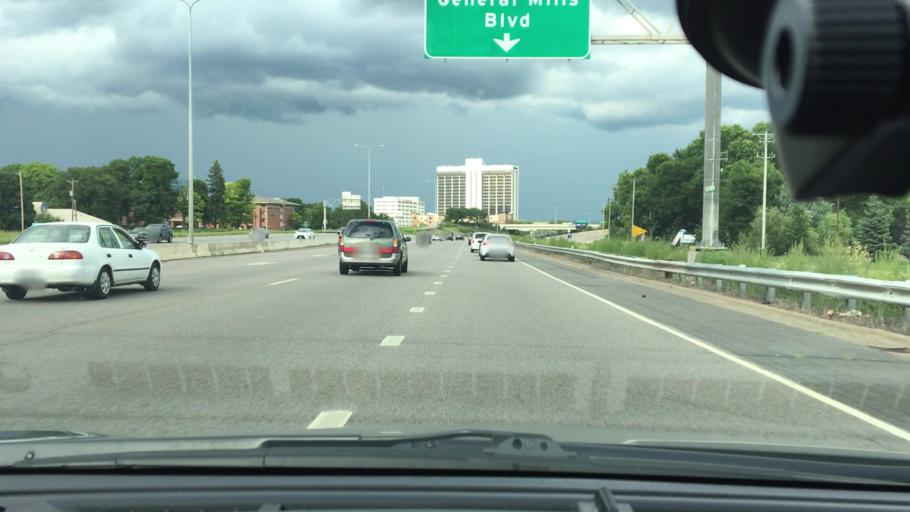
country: US
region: Minnesota
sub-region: Hennepin County
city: Minnetonka Mills
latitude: 44.9721
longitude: -93.4145
